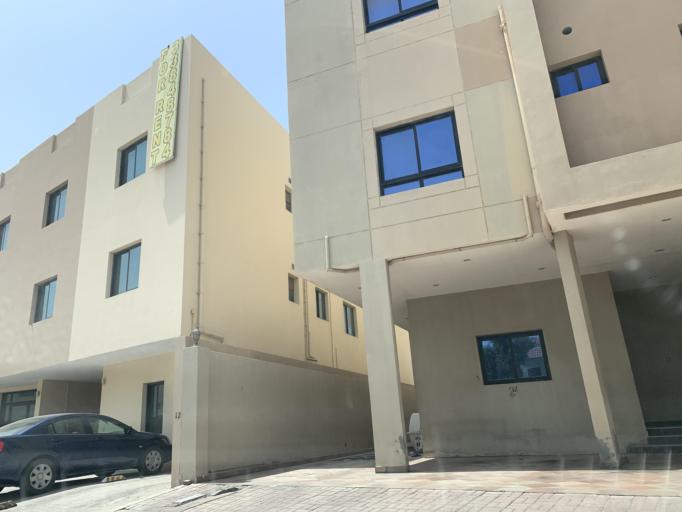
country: BH
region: Manama
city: Jidd Hafs
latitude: 26.2016
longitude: 50.5636
